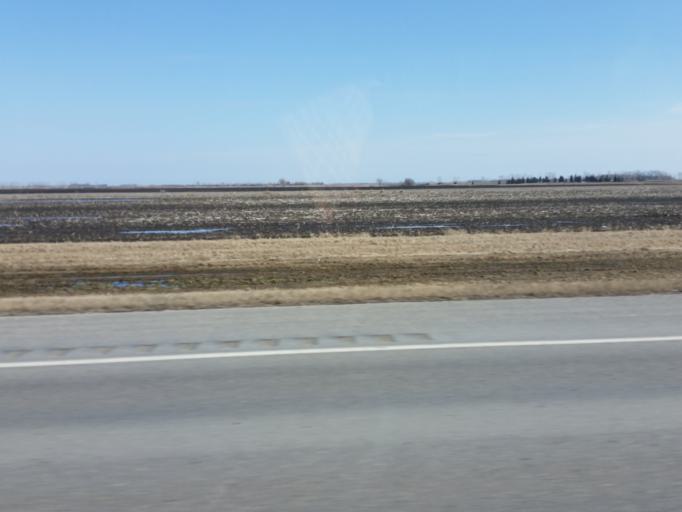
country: US
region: North Dakota
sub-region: Walsh County
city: Grafton
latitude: 48.2258
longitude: -97.3623
